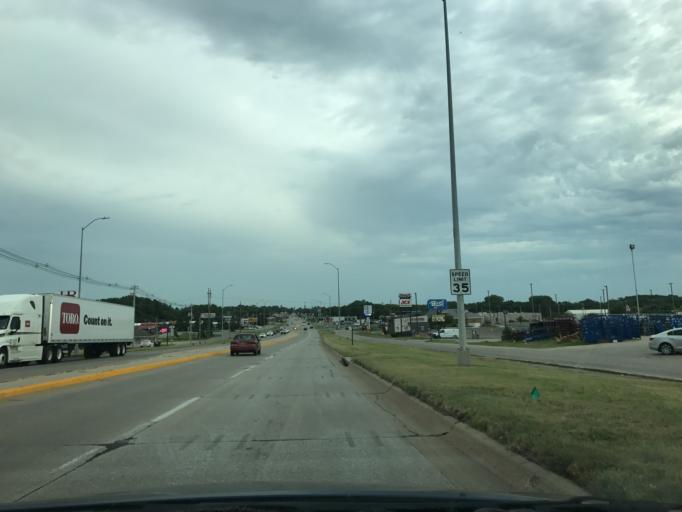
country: US
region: Nebraska
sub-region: Gage County
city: Beatrice
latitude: 40.2916
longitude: -96.7466
